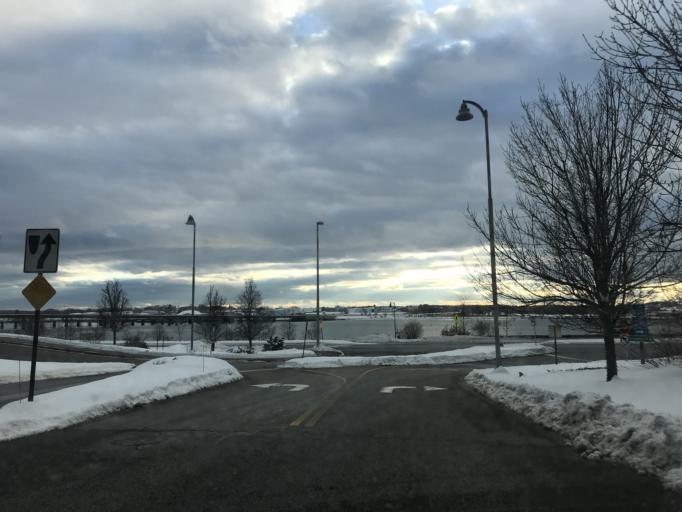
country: US
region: Maine
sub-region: Cumberland County
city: Portland
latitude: 43.6490
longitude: -70.2831
